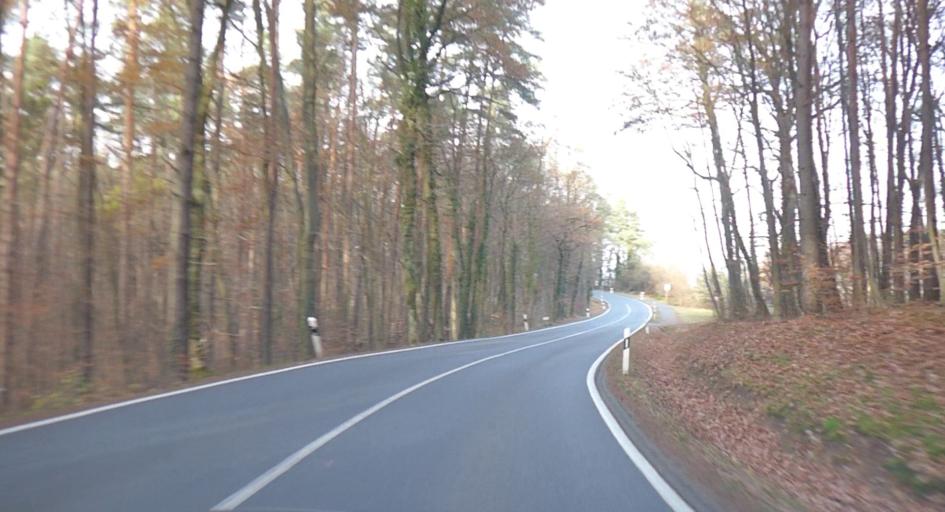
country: DE
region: Bavaria
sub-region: Regierungsbezirk Mittelfranken
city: Bubenreuth
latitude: 49.6263
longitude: 11.0389
